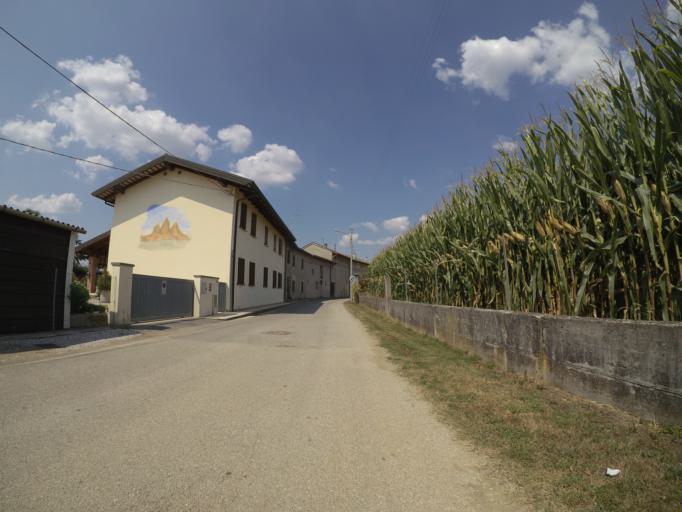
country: IT
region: Friuli Venezia Giulia
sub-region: Provincia di Udine
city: Bertiolo
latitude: 45.9350
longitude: 13.0713
